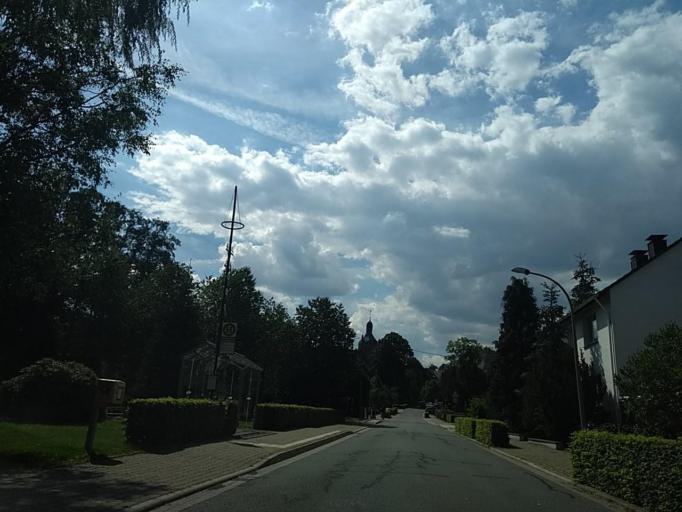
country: DE
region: North Rhine-Westphalia
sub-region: Regierungsbezirk Arnsberg
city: Brilon
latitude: 51.4578
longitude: 8.6252
